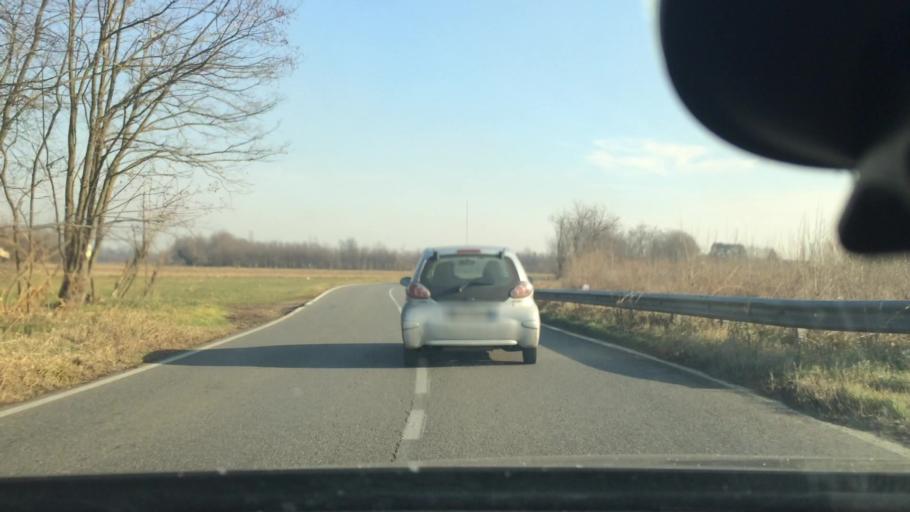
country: IT
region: Lombardy
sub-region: Citta metropolitana di Milano
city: Casorezzo
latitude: 45.5128
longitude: 8.9218
